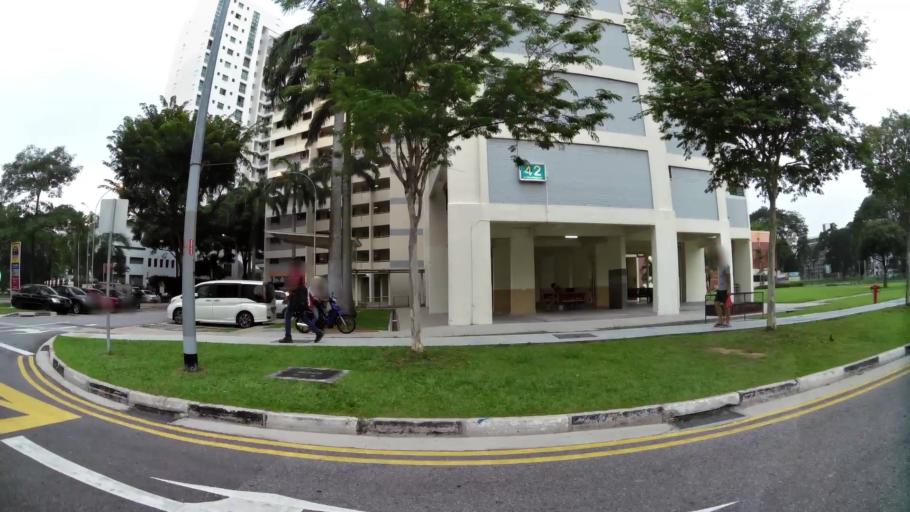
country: SG
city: Singapore
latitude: 1.3103
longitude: 103.8861
